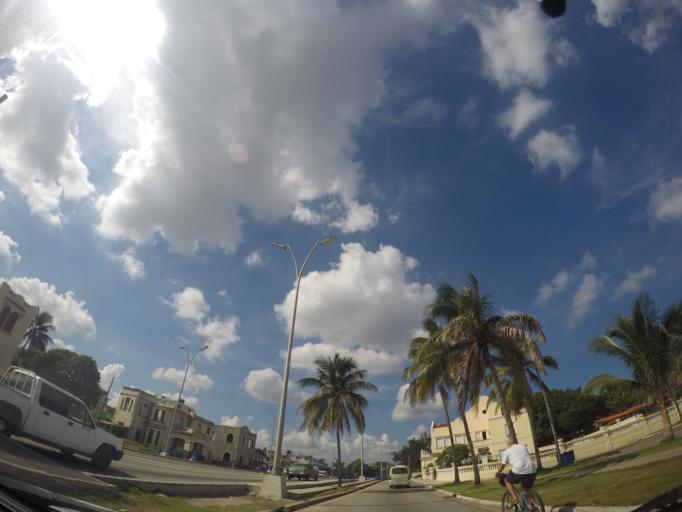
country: CU
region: La Habana
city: Havana
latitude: 23.1315
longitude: -82.4092
